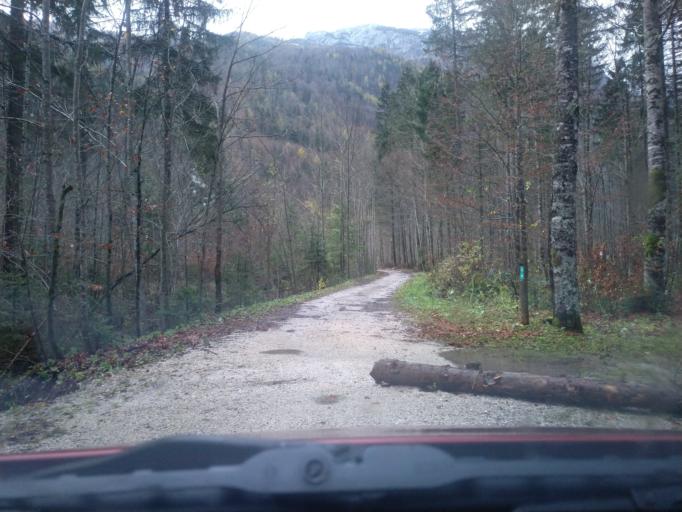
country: SI
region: Solcava
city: Solcava
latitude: 46.3997
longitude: 14.6290
